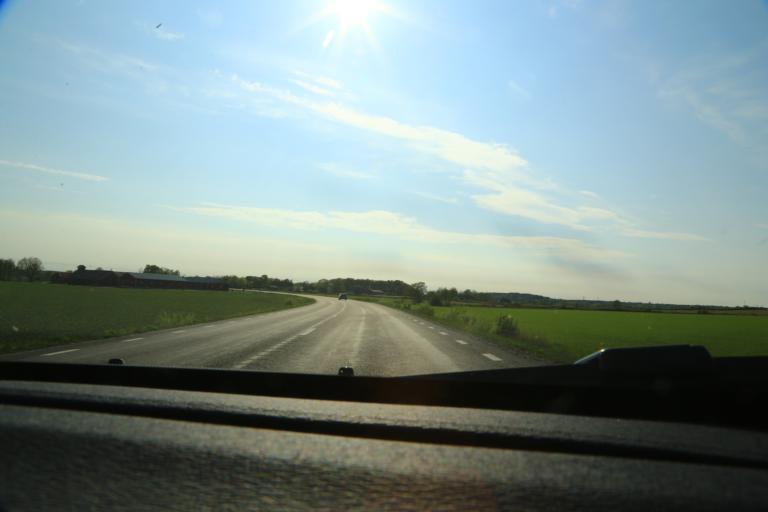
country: SE
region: Halland
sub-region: Kungsbacka Kommun
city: Frillesas
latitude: 57.2464
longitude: 12.2040
